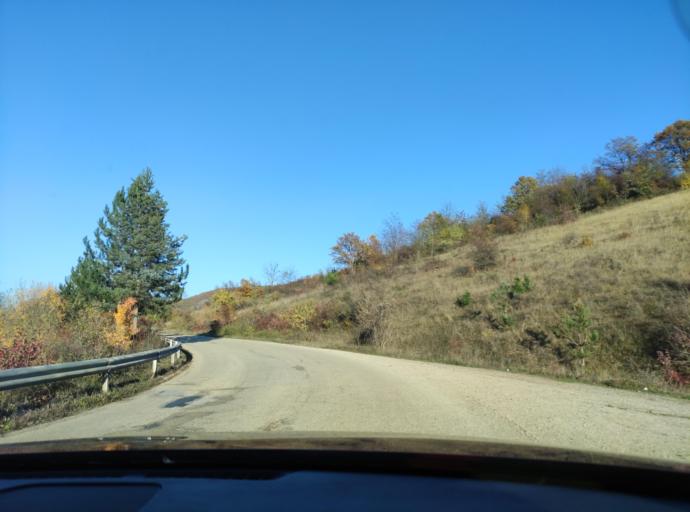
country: BG
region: Montana
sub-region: Obshtina Chiprovtsi
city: Chiprovtsi
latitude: 43.3790
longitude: 22.9138
